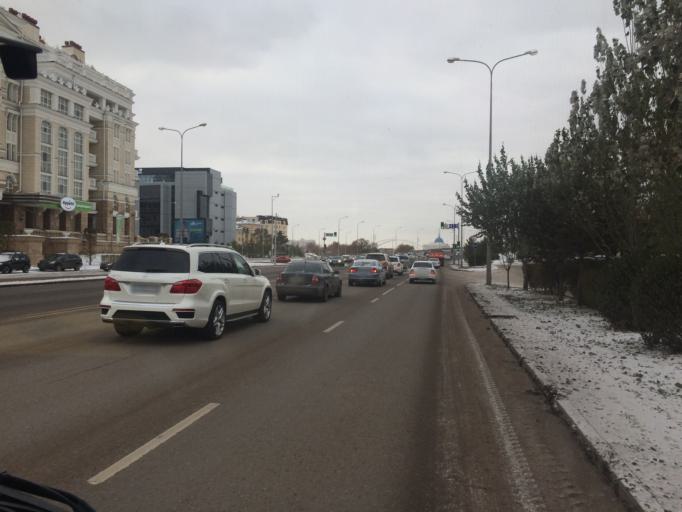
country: KZ
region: Astana Qalasy
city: Astana
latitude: 51.1428
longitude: 71.4450
